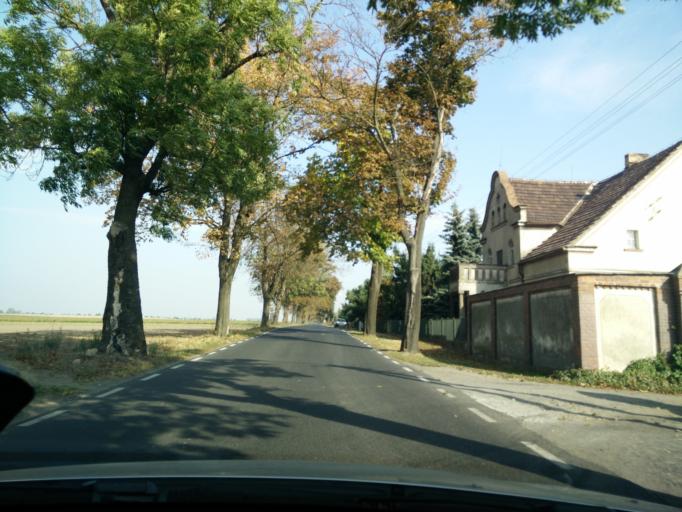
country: PL
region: Greater Poland Voivodeship
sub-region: Powiat sredzki
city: Sroda Wielkopolska
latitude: 52.2450
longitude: 17.2924
